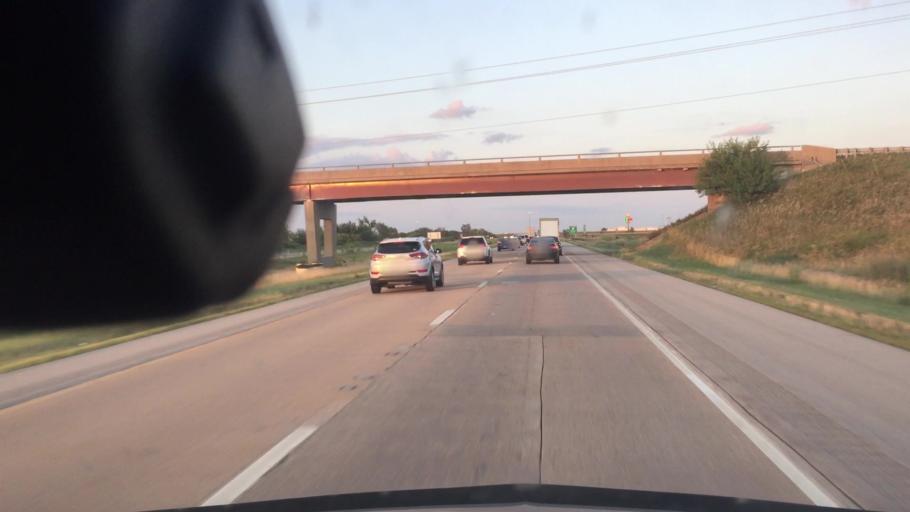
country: US
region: Illinois
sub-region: Livingston County
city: Dwight
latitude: 41.1138
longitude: -88.4338
